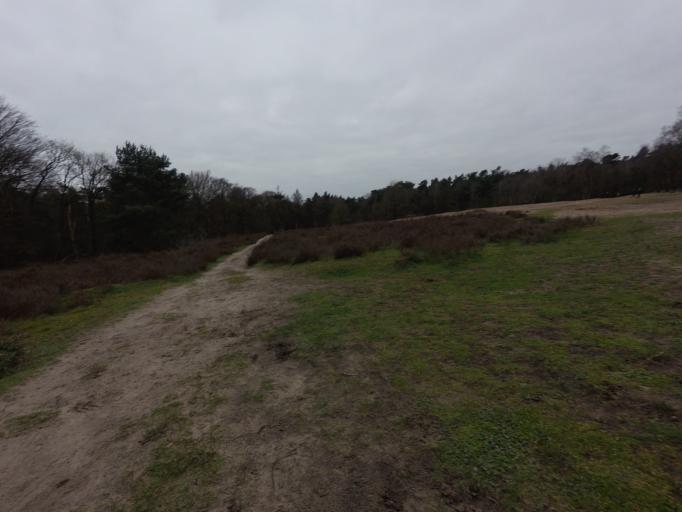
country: NL
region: Utrecht
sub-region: Gemeente Utrechtse Heuvelrug
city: Doorn
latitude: 52.0441
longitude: 5.3530
